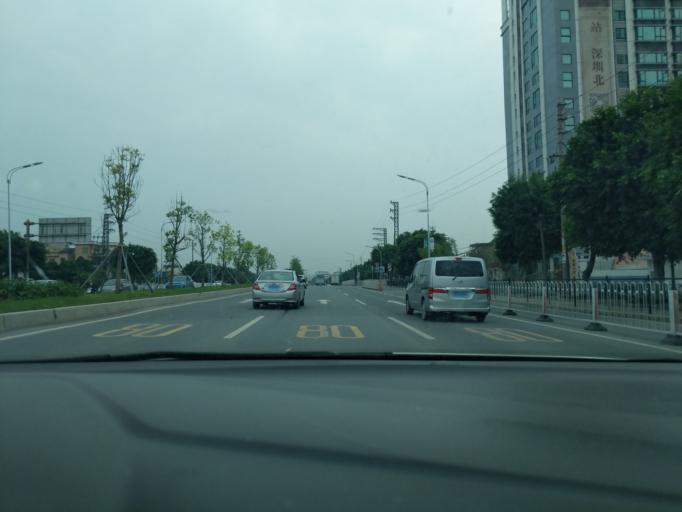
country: CN
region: Guangdong
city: Dongyong
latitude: 22.8643
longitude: 113.4819
